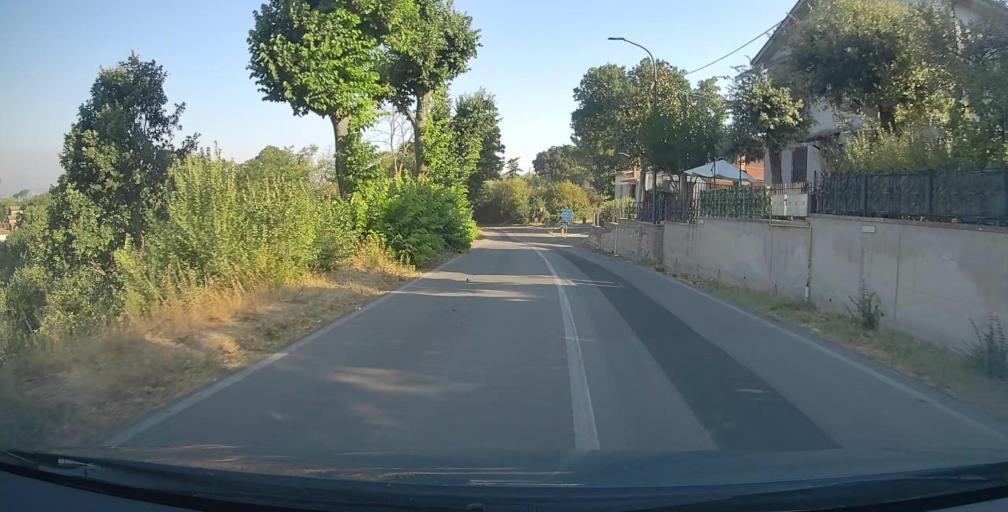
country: IT
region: Umbria
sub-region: Provincia di Terni
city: Calvi dell'Umbria
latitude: 42.3930
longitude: 12.5650
